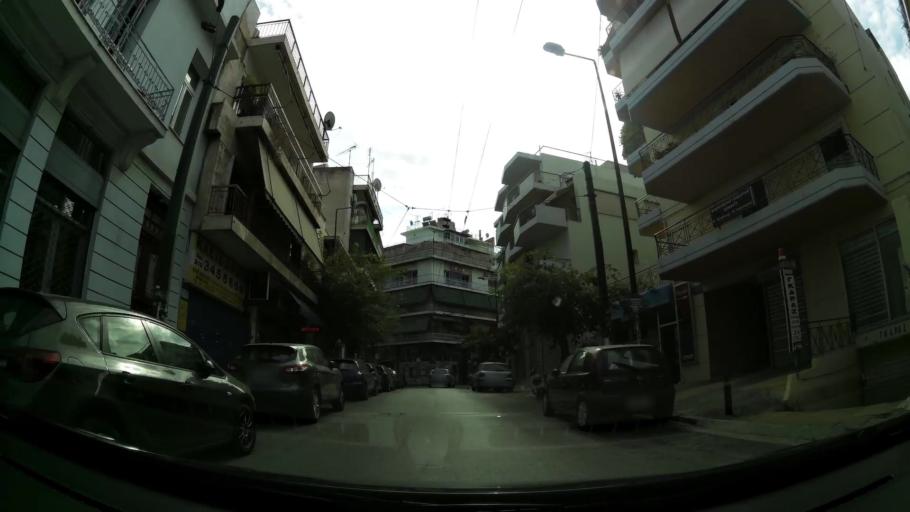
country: GR
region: Attica
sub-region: Nomarchia Athinas
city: Athens
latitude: 37.9757
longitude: 23.7140
